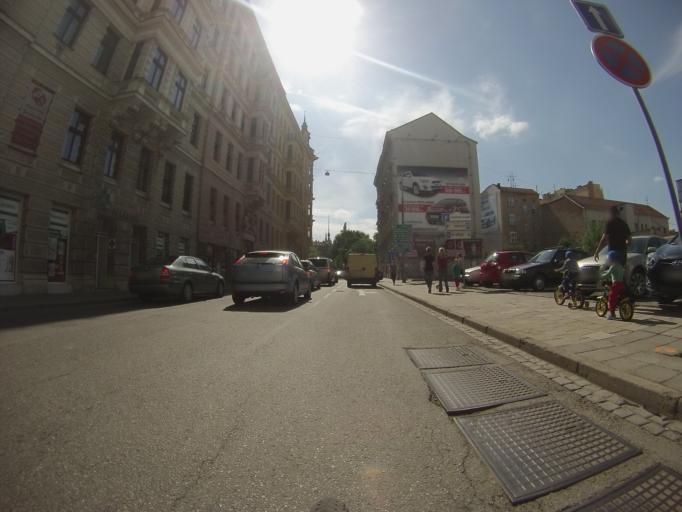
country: CZ
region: South Moravian
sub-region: Mesto Brno
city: Brno
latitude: 49.1985
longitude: 16.6150
